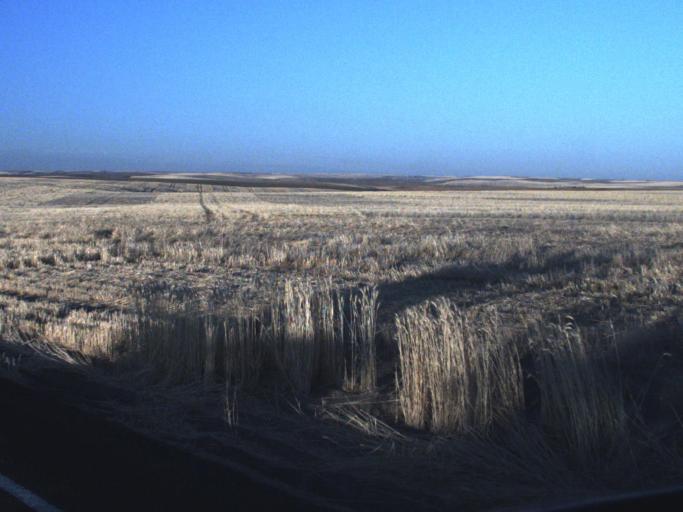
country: US
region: Washington
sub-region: Adams County
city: Ritzville
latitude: 46.9247
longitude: -118.5671
